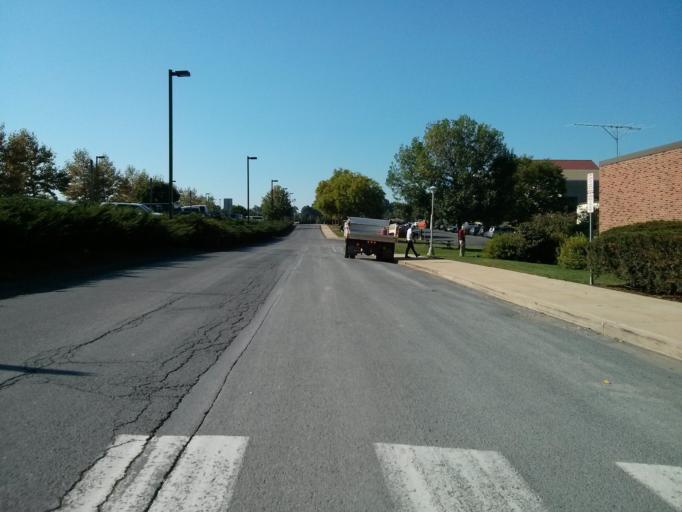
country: US
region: Pennsylvania
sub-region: Centre County
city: State College
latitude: 40.8088
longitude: -77.8673
